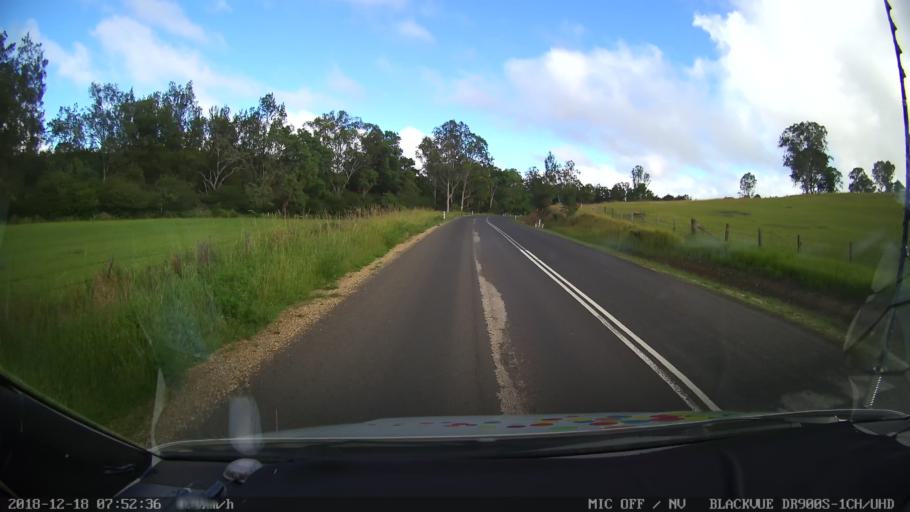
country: AU
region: New South Wales
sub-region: Kyogle
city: Kyogle
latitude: -28.4267
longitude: 152.5810
